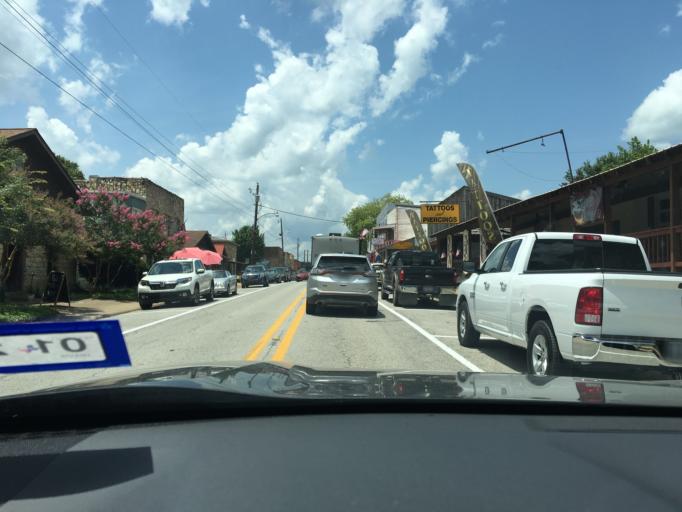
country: US
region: Arkansas
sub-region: Sharp County
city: Cherokee Village
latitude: 36.3157
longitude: -91.4803
